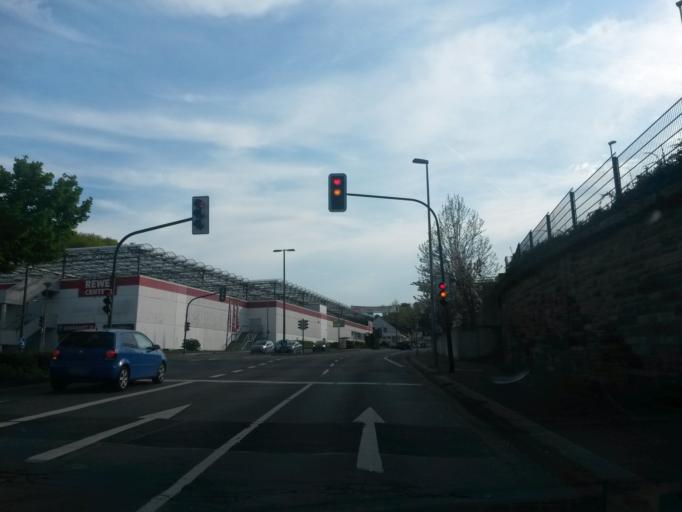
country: DE
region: North Rhine-Westphalia
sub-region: Regierungsbezirk Arnsberg
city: Luedenscheid
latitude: 51.2269
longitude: 7.6345
